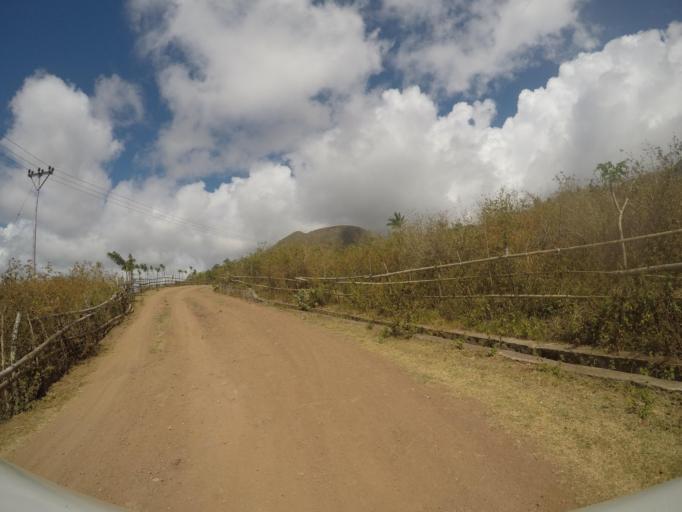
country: TL
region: Lautem
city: Lospalos
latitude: -8.5386
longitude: 126.8062
